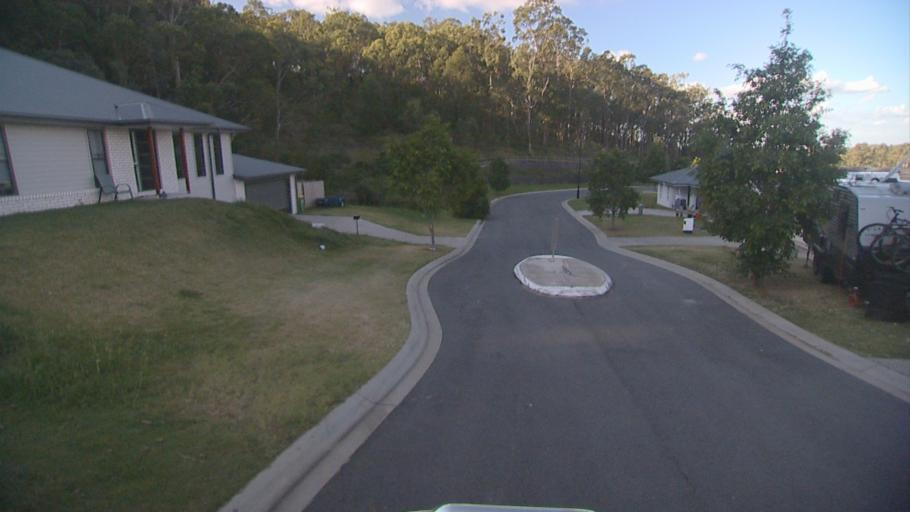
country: AU
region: Queensland
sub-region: Logan
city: Windaroo
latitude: -27.7487
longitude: 153.1827
